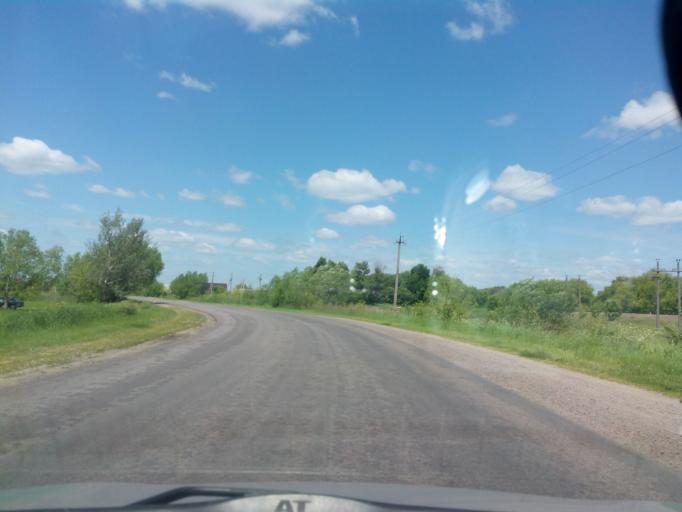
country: RU
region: Voronezj
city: Ternovka
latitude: 51.6885
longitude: 41.5792
